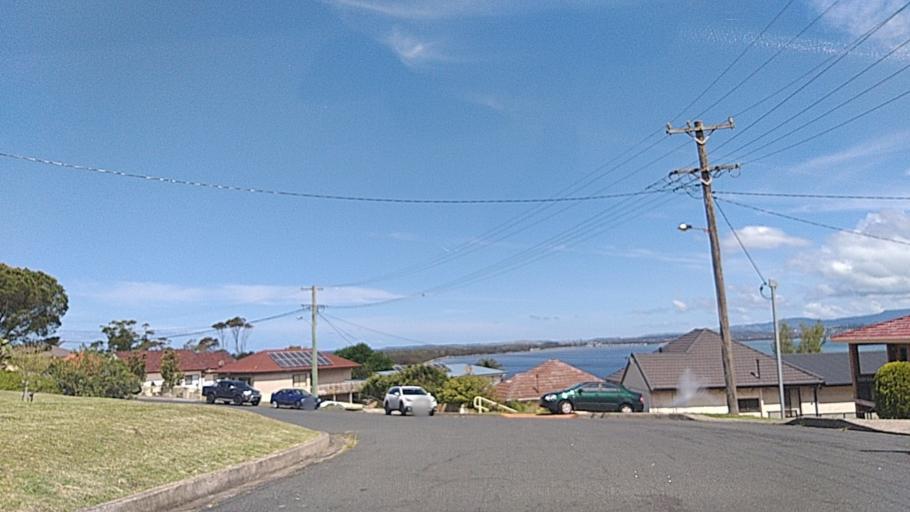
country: AU
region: New South Wales
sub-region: Wollongong
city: Lake Heights
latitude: -34.4895
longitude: 150.8701
